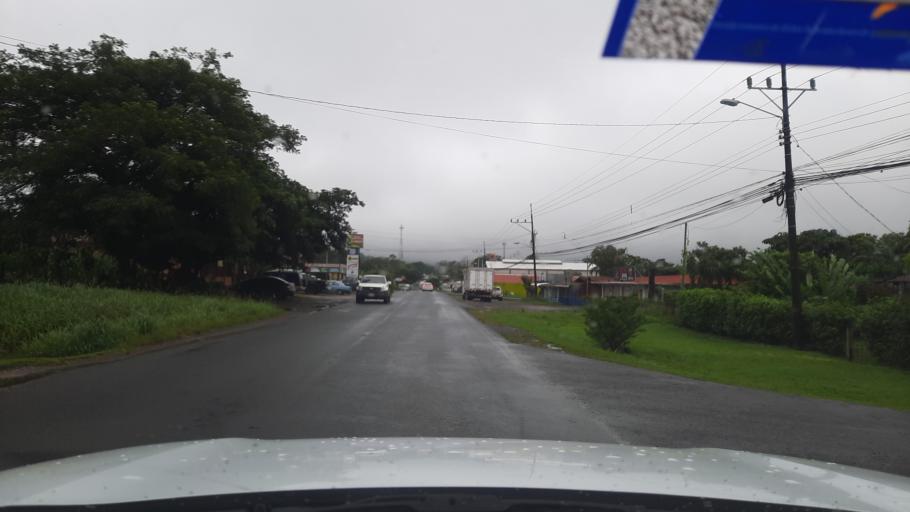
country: CR
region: Alajuela
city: Bijagua
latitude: 10.7331
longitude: -85.0525
